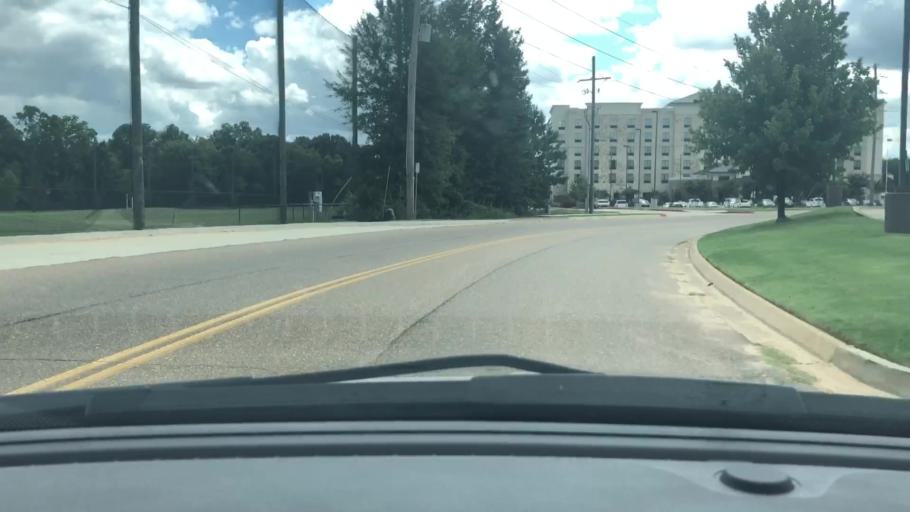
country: US
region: Arkansas
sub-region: Miller County
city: Texarkana
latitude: 33.4595
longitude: -94.0741
